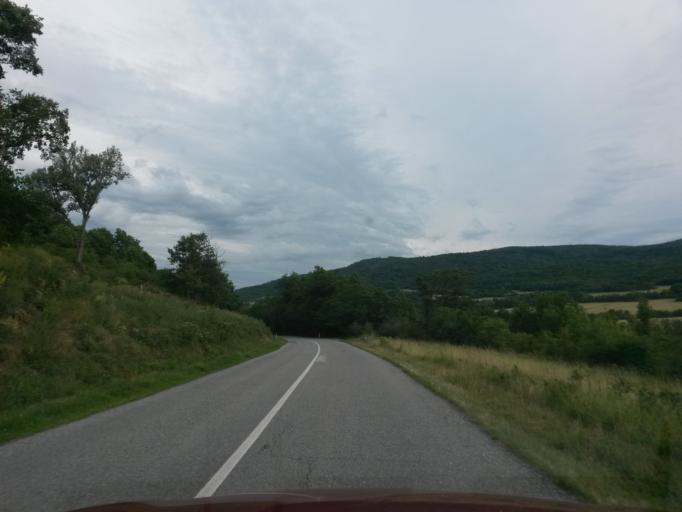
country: SK
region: Banskobystricky
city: Detva
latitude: 48.3966
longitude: 19.3752
